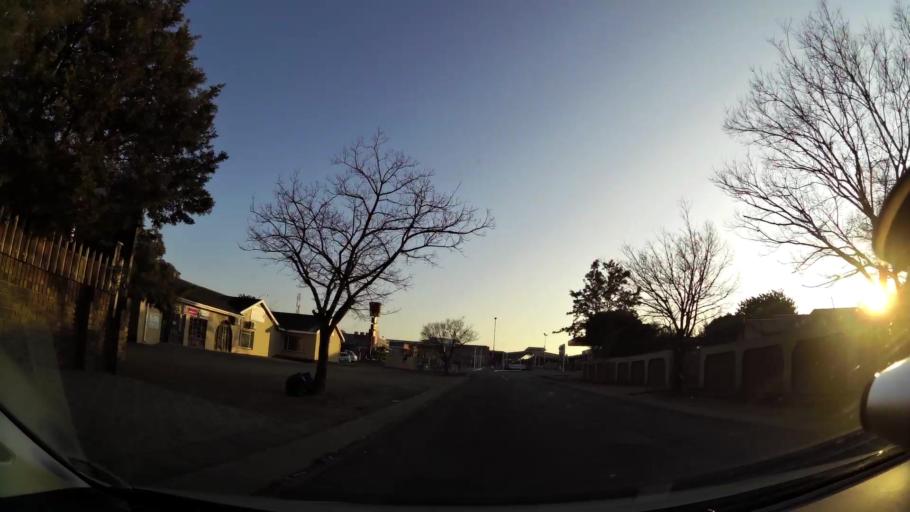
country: ZA
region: Orange Free State
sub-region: Mangaung Metropolitan Municipality
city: Bloemfontein
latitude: -29.1020
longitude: 26.1588
